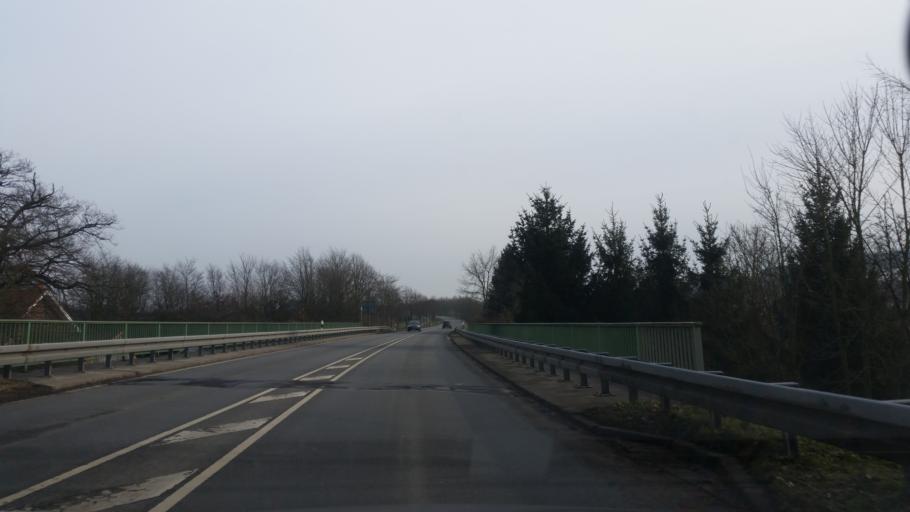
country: DE
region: North Rhine-Westphalia
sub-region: Regierungsbezirk Detmold
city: Barntrup
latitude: 52.0696
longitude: 9.1344
